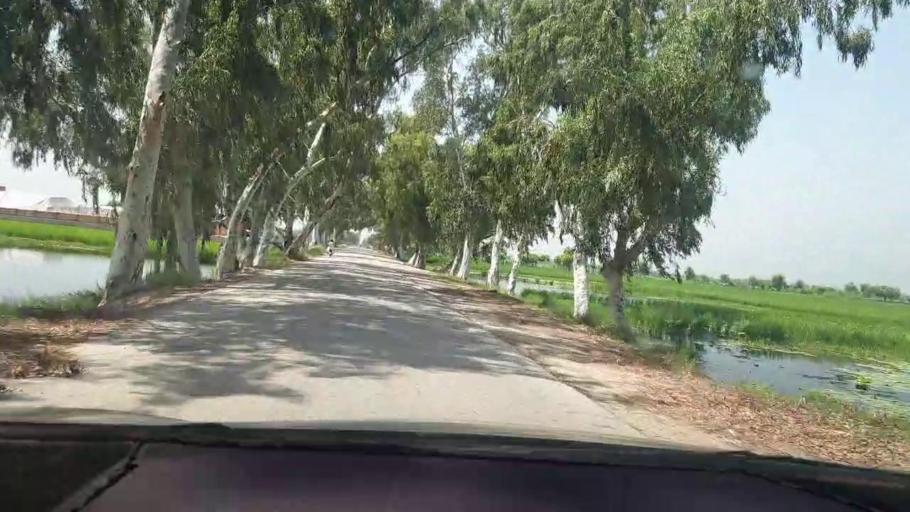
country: PK
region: Sindh
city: Kambar
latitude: 27.6035
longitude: 68.0339
